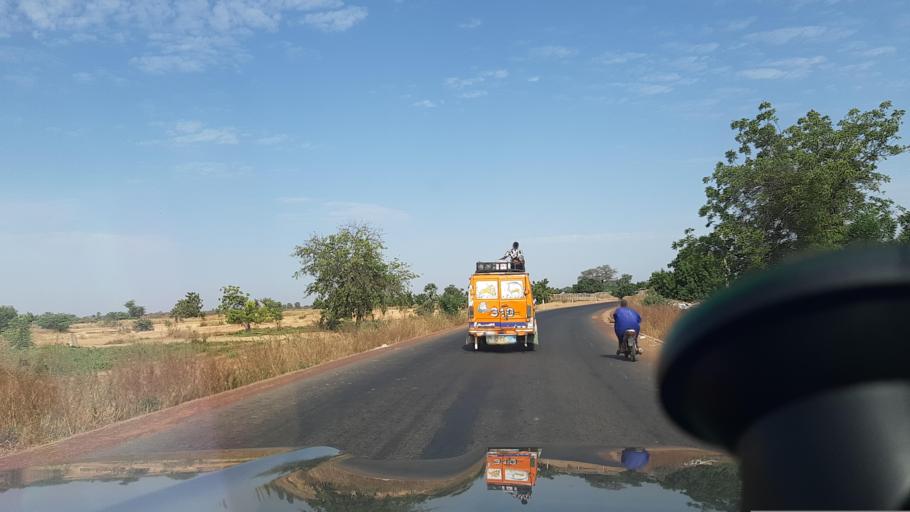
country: ML
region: Segou
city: Markala
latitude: 13.6873
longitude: -6.0997
